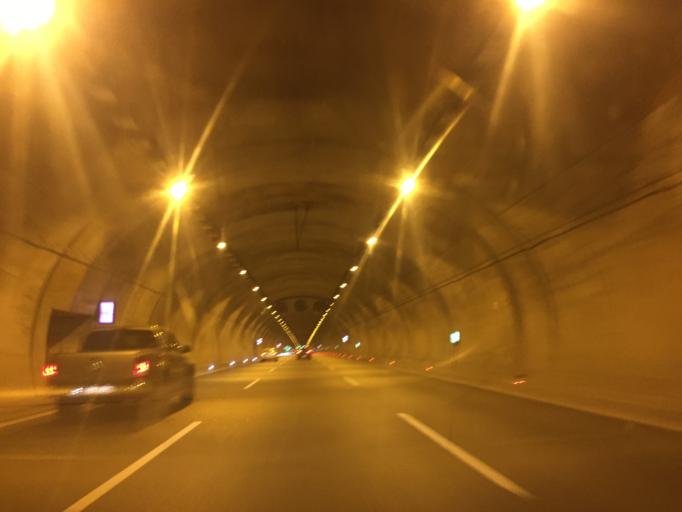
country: TR
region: Bursa
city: Demirtas
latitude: 40.3245
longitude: 29.0951
